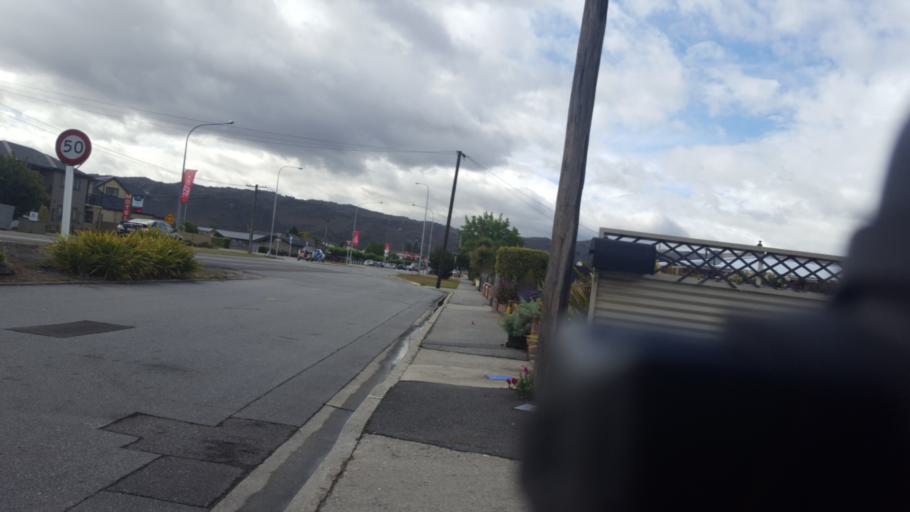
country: NZ
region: Otago
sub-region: Queenstown-Lakes District
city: Wanaka
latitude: -45.2473
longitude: 169.3834
